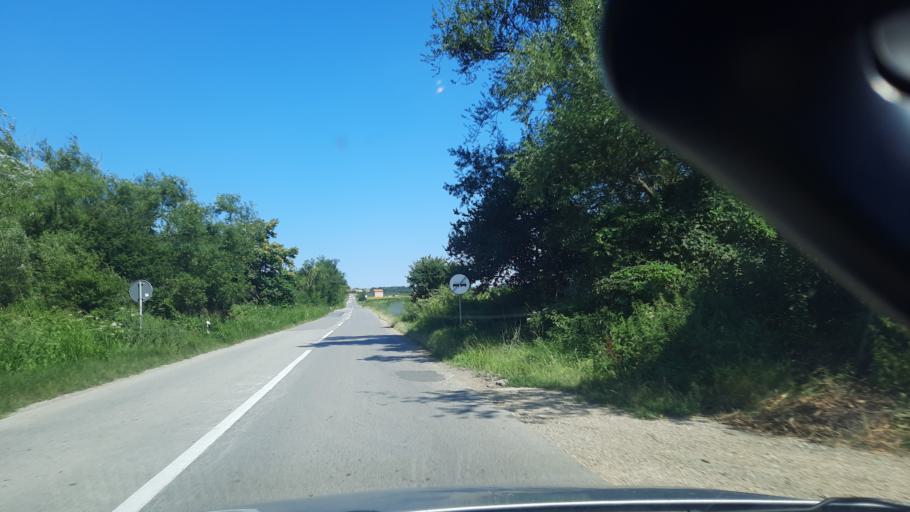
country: RS
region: Central Serbia
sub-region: Branicevski Okrug
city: Malo Crnice
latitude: 44.5763
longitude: 21.3423
